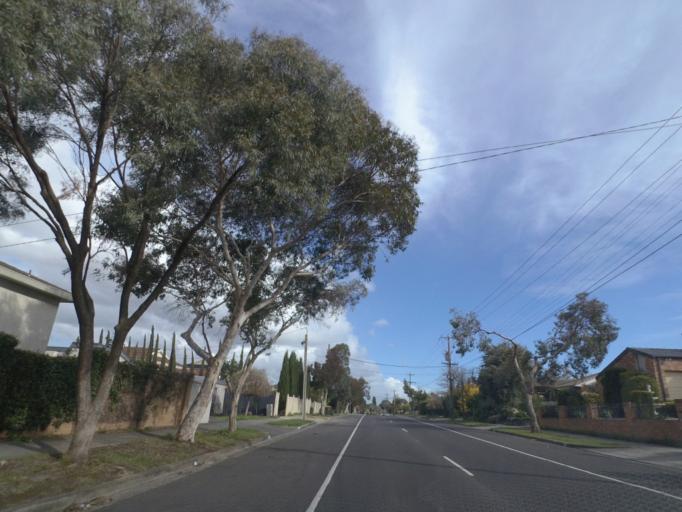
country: AU
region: Victoria
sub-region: Whitehorse
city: Vermont South
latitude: -37.8555
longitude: 145.1906
